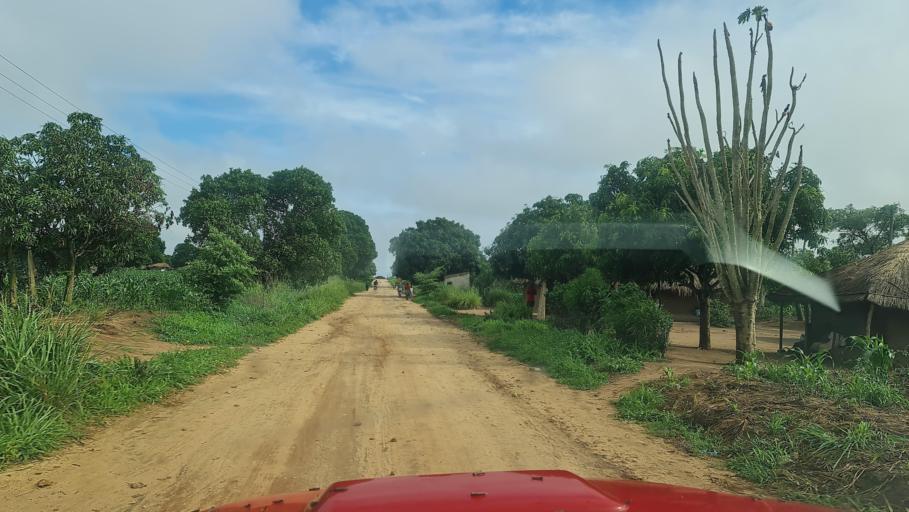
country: MW
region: Southern Region
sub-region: Nsanje District
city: Nsanje
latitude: -17.3031
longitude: 35.5934
